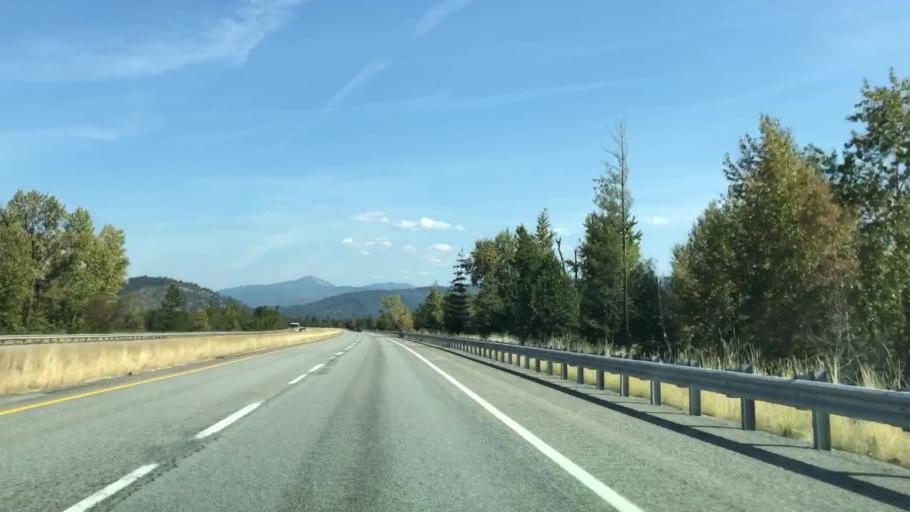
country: US
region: Idaho
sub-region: Shoshone County
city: Pinehurst
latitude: 47.5591
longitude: -116.3916
